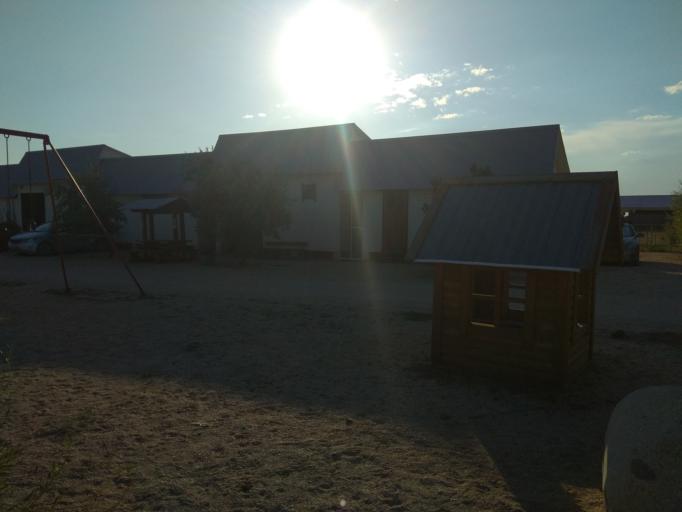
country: RU
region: Krasnodarskiy
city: Dolzhanskaya
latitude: 46.6805
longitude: 37.7381
